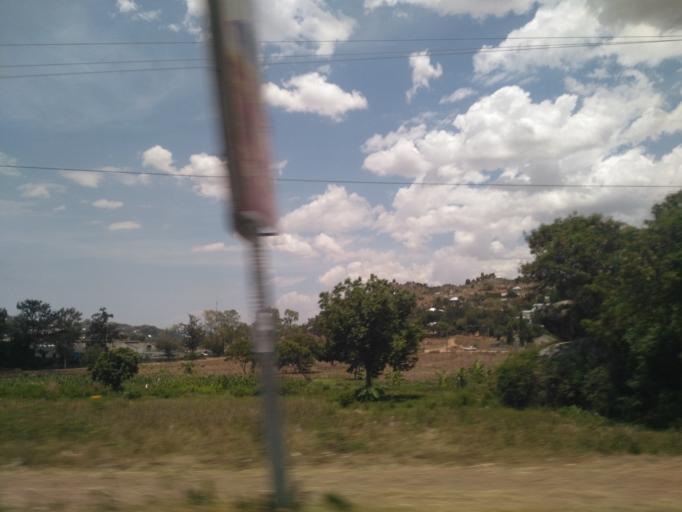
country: TZ
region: Mwanza
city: Mwanza
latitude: -2.5719
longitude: 32.9194
